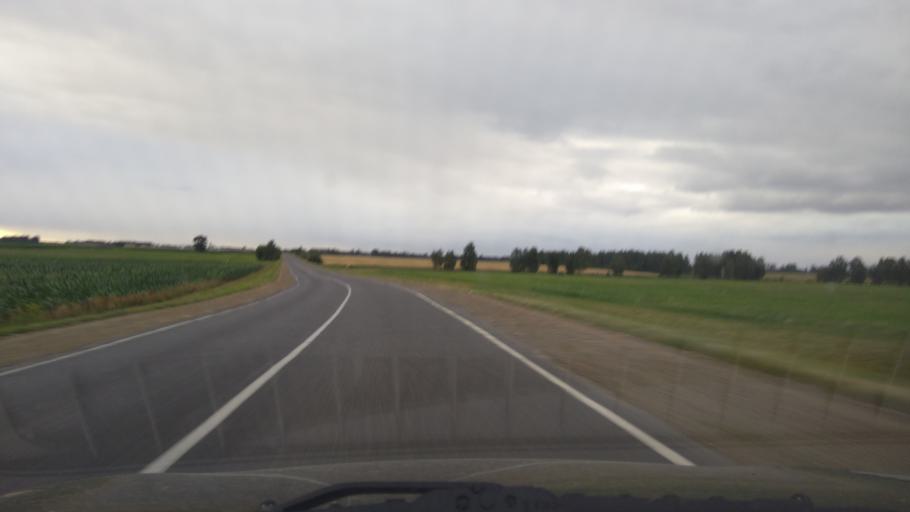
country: BY
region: Brest
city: Byaroza
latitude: 52.4351
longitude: 24.9800
